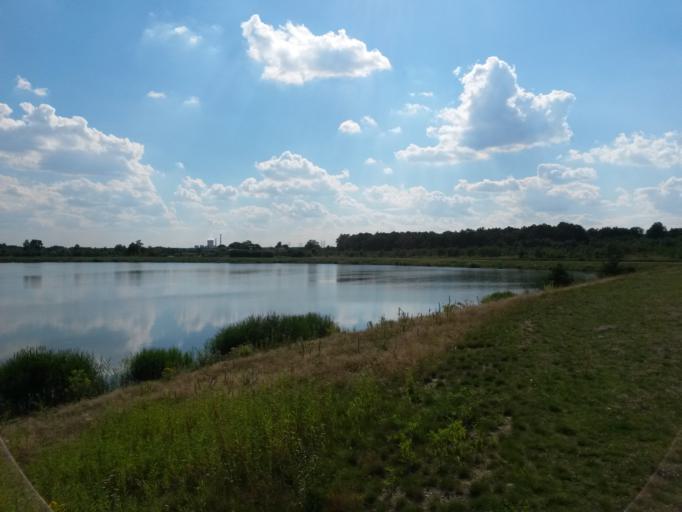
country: PL
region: Silesian Voivodeship
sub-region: Powiat bedzinski
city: Sarnow
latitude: 50.3833
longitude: 19.1989
